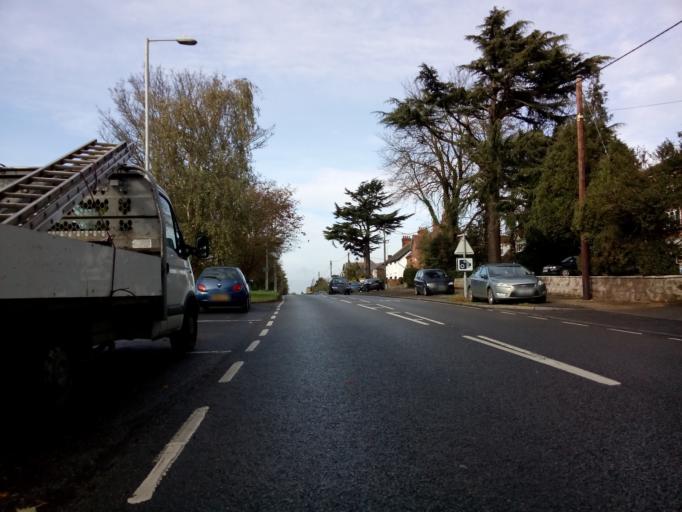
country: GB
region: England
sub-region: Suffolk
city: Needham Market
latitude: 52.1585
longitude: 1.0467
